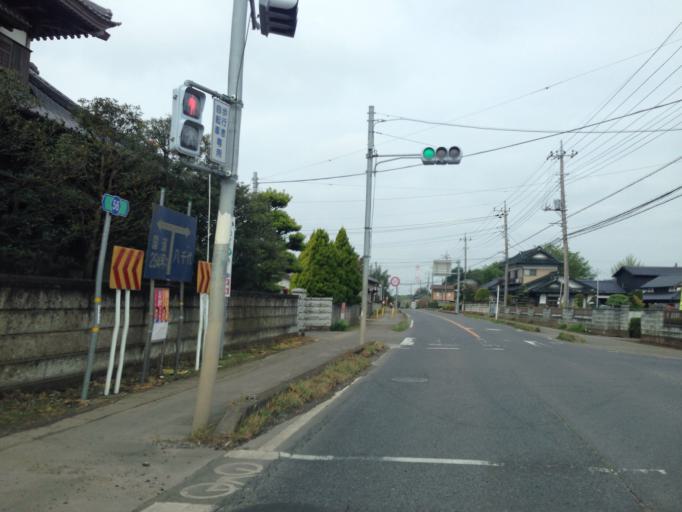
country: JP
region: Ibaraki
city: Ishige
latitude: 36.1587
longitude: 139.9345
